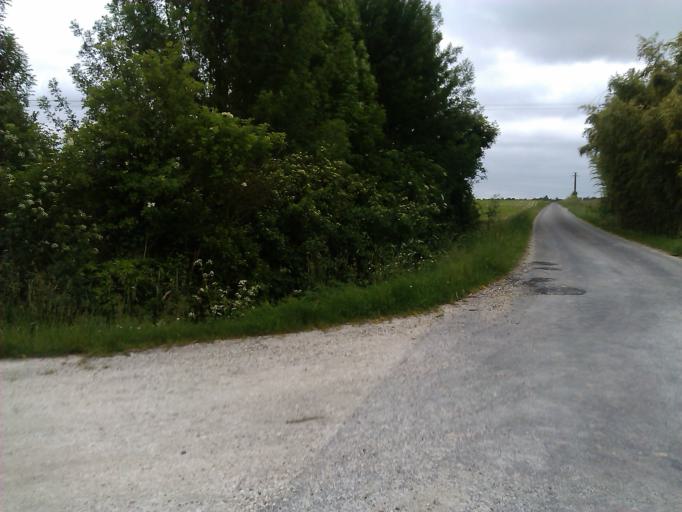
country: FR
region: Poitou-Charentes
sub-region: Departement de la Charente
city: Barbezieux-Saint-Hilaire
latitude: 45.4935
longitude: -0.1336
